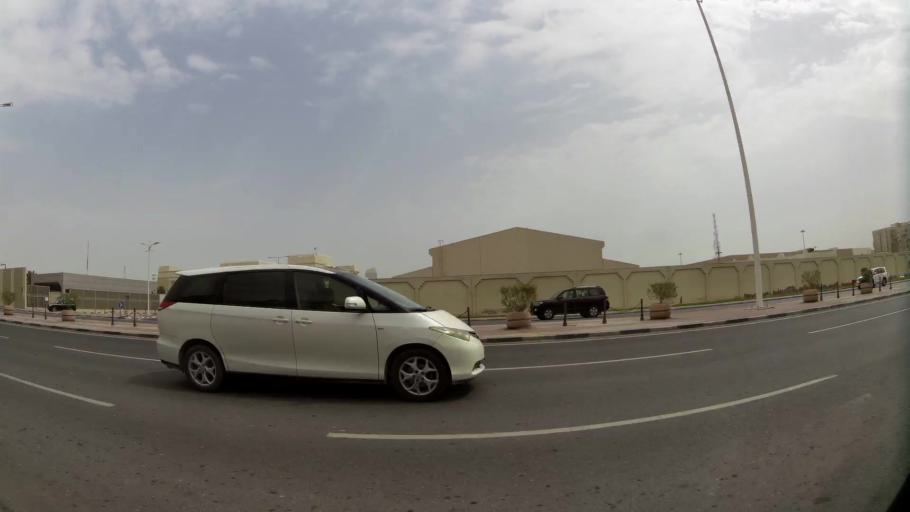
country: QA
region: Baladiyat ad Dawhah
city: Doha
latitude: 25.3020
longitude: 51.5009
